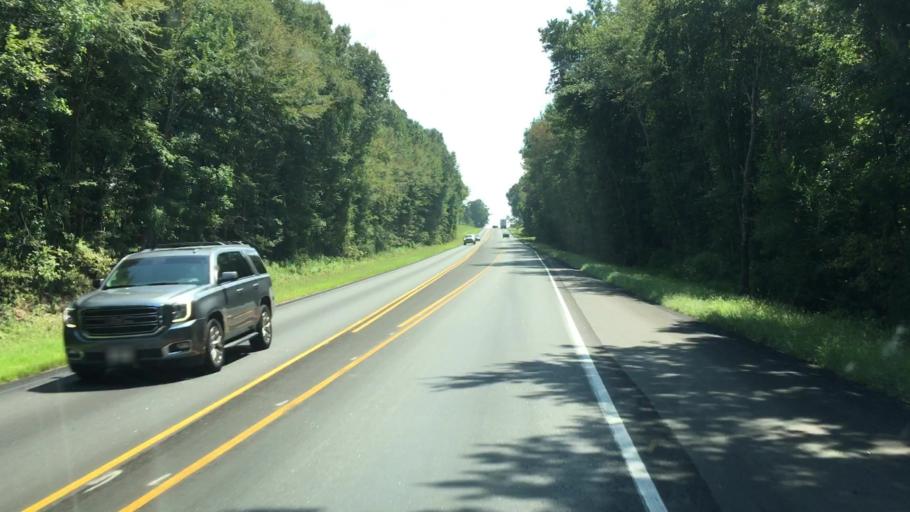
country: US
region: Georgia
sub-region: Morgan County
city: Madison
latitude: 33.6627
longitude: -83.4453
